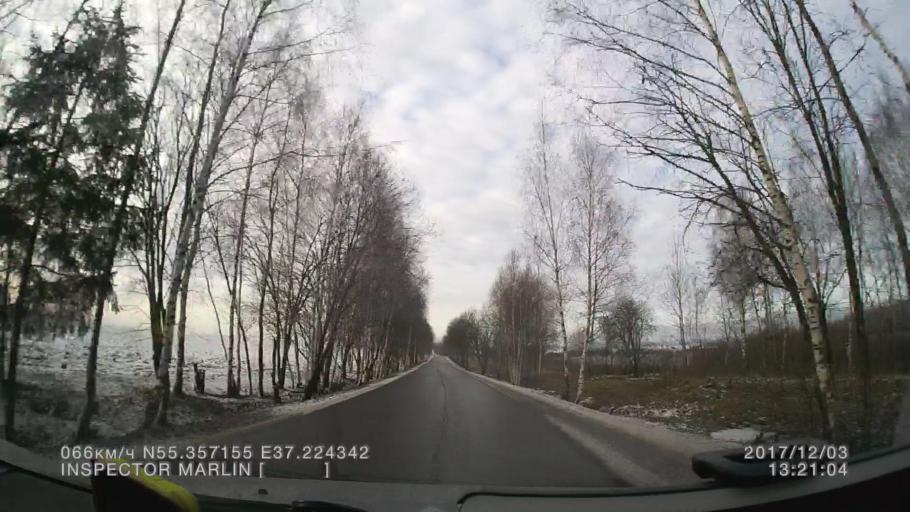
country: RU
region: Moskovskaya
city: Troitsk
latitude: 55.3572
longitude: 37.2243
